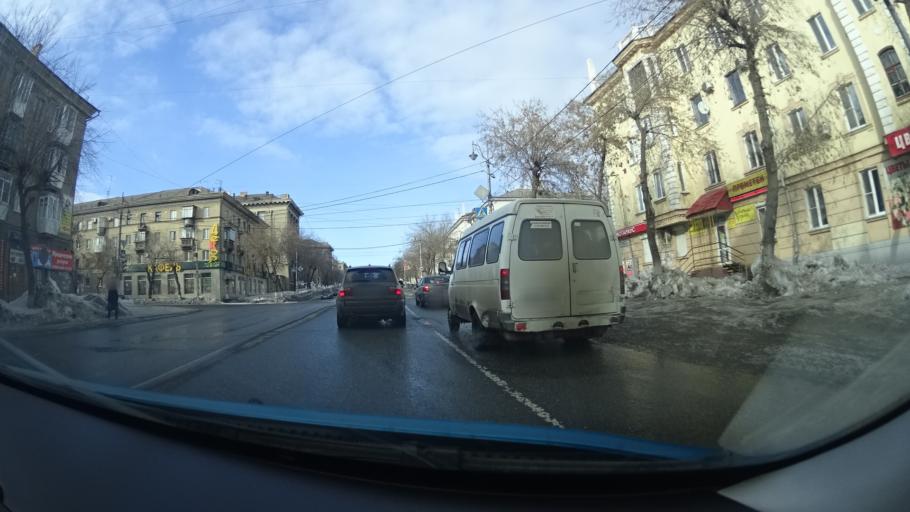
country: RU
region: Chelyabinsk
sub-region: Gorod Magnitogorsk
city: Magnitogorsk
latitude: 53.4256
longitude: 58.9837
